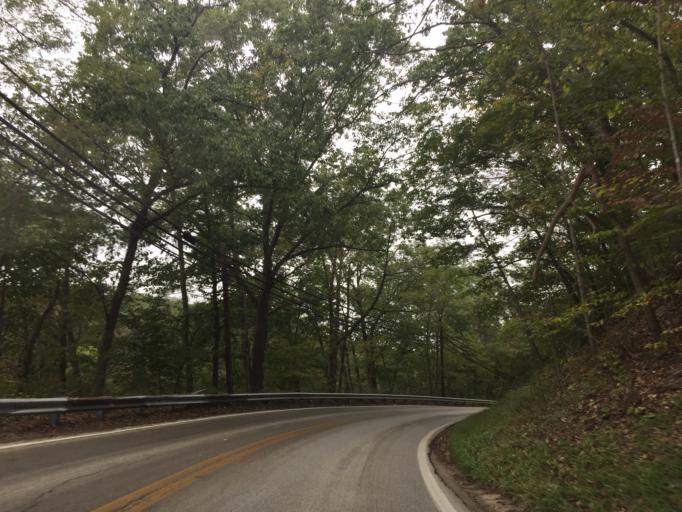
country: US
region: Maryland
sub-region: Baltimore County
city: Cockeysville
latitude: 39.4859
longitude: -76.6128
